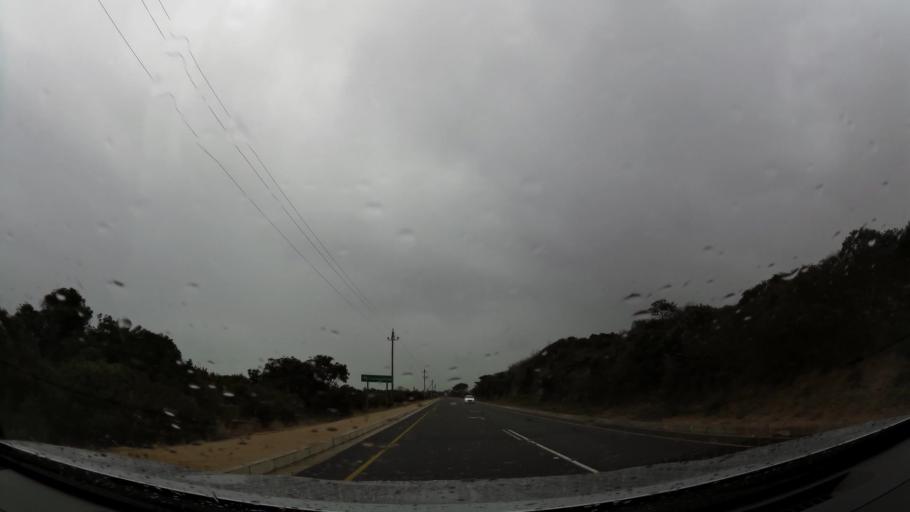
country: ZA
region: Western Cape
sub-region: Eden District Municipality
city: Mossel Bay
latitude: -34.0492
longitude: 22.2776
